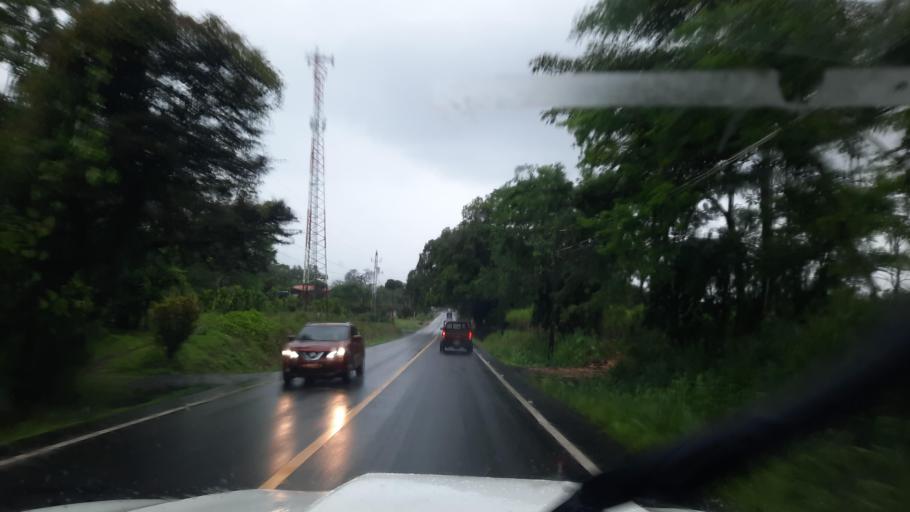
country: PA
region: Chiriqui
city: Sortova
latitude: 8.5542
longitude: -82.6267
